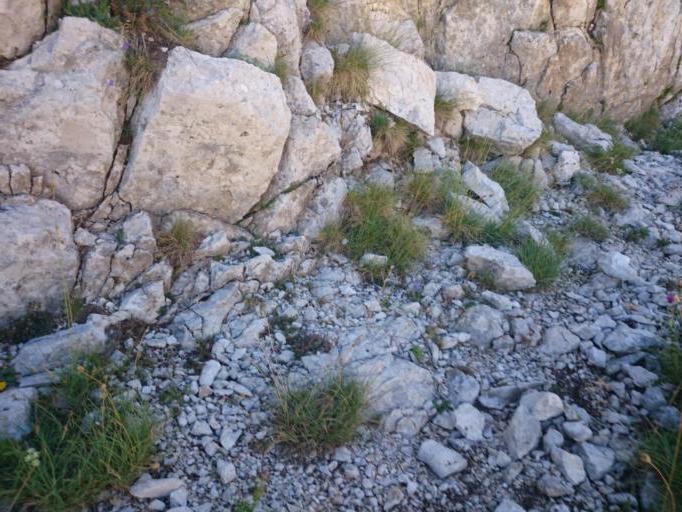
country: AL
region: Elbasan
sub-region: Rrethi i Gramshit
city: Kushove
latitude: 40.7135
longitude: 20.1506
